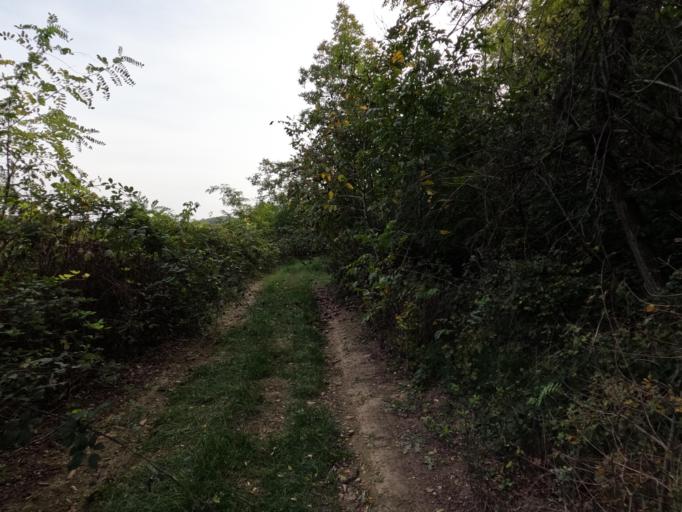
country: HU
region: Tolna
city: Szentgalpuszta
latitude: 46.3390
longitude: 18.6481
